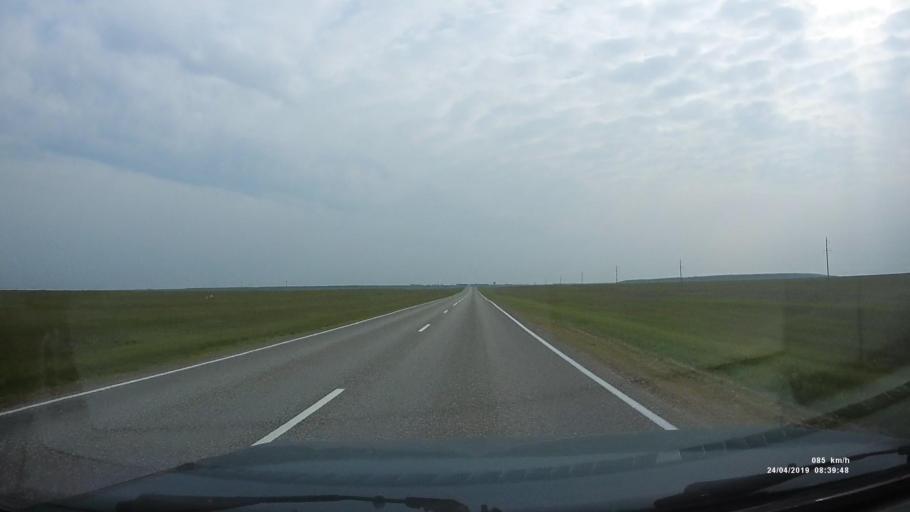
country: RU
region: Kalmykiya
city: Arshan'
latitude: 46.2229
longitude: 43.9902
